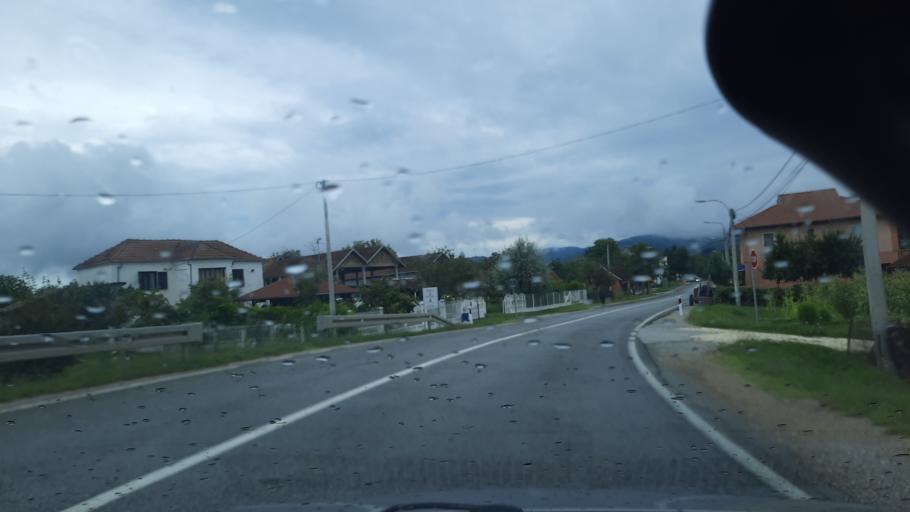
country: RS
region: Central Serbia
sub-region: Sumadijski Okrug
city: Knic
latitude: 43.8989
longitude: 20.7678
